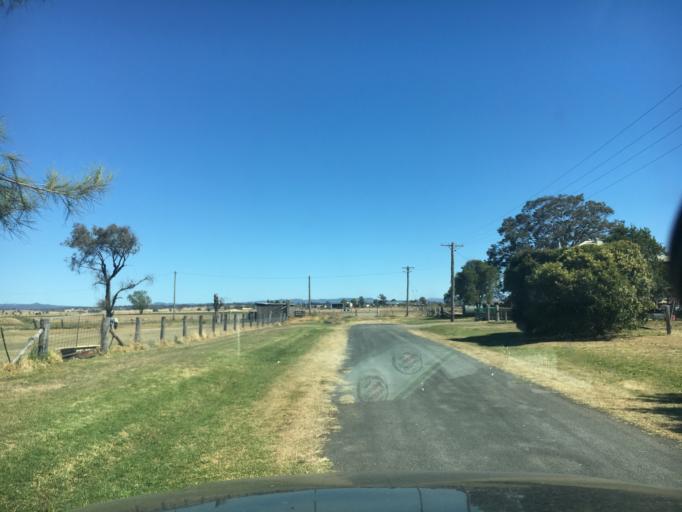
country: AU
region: New South Wales
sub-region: Singleton
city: Singleton
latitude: -32.5760
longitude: 151.1667
